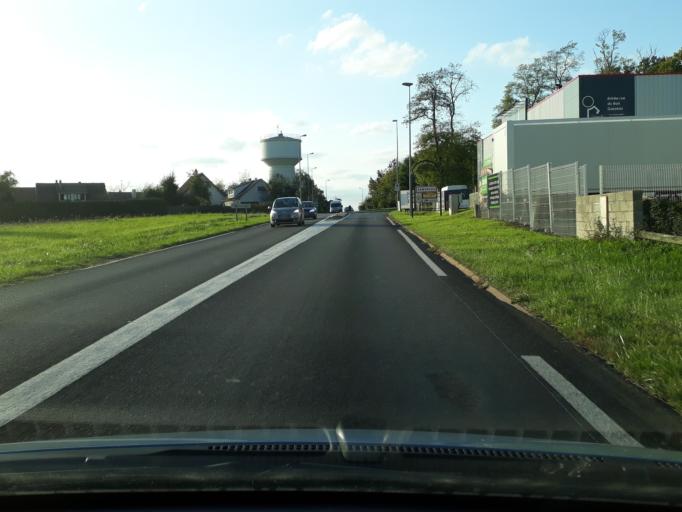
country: FR
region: Ile-de-France
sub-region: Departement de Seine-et-Marne
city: Vulaines-sur-Seine
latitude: 48.4246
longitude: 2.7632
